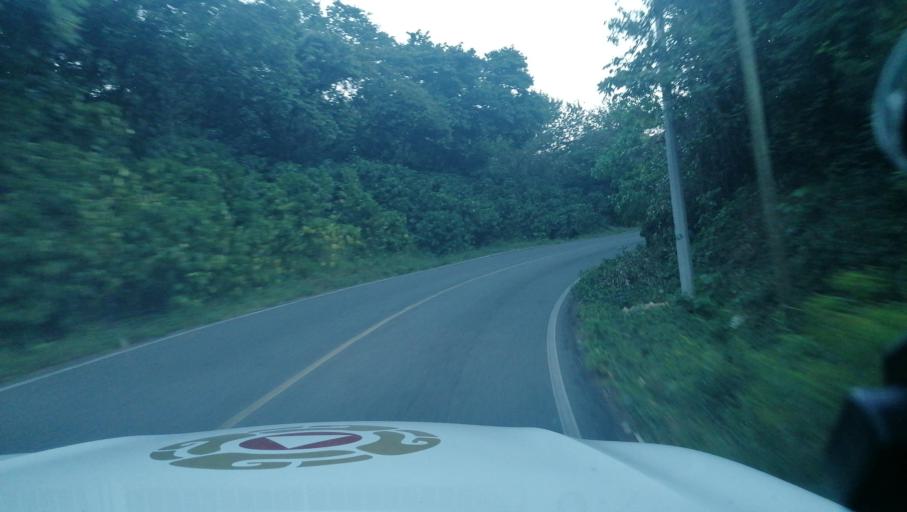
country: MX
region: Chiapas
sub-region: Cacahoatan
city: Benito Juarez
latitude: 15.0366
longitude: -92.2424
